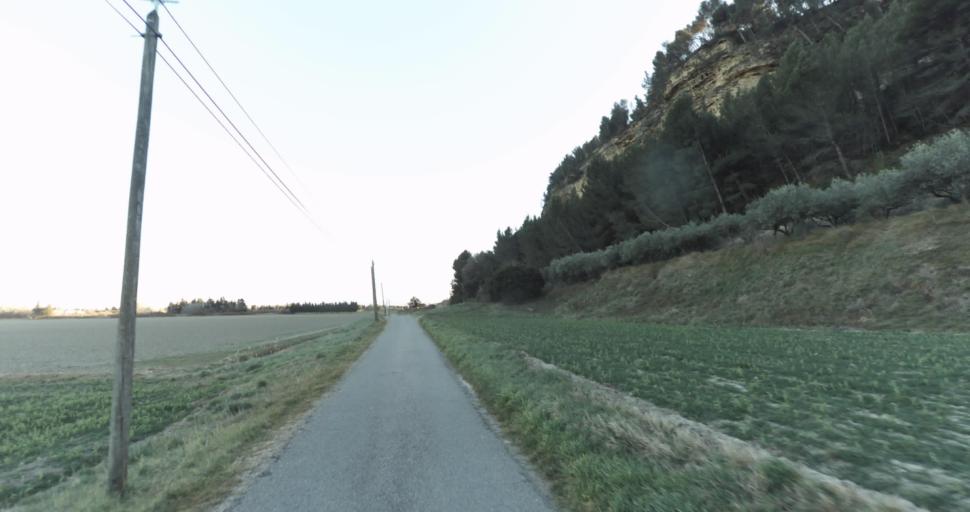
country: FR
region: Provence-Alpes-Cote d'Azur
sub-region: Departement des Bouches-du-Rhone
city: Barbentane
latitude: 43.8952
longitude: 4.7657
